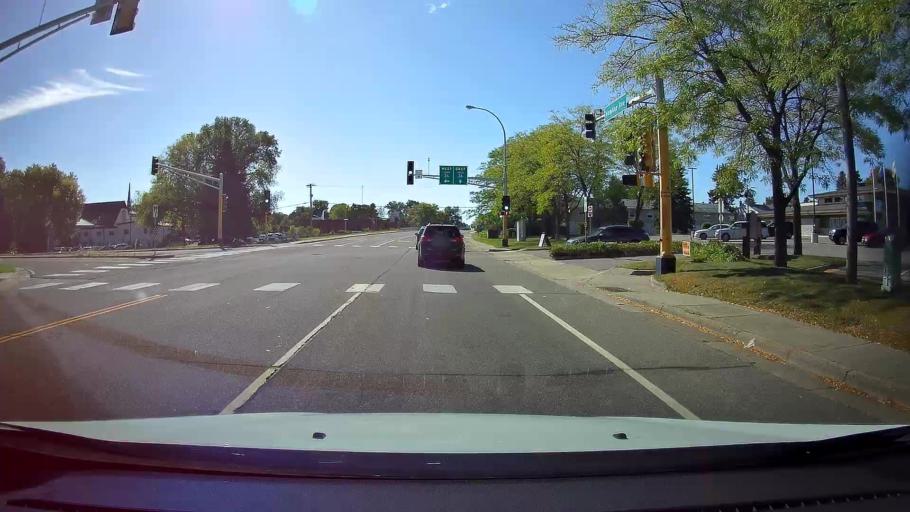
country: US
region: Minnesota
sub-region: Ramsey County
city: Roseville
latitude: 45.0122
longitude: -93.1567
